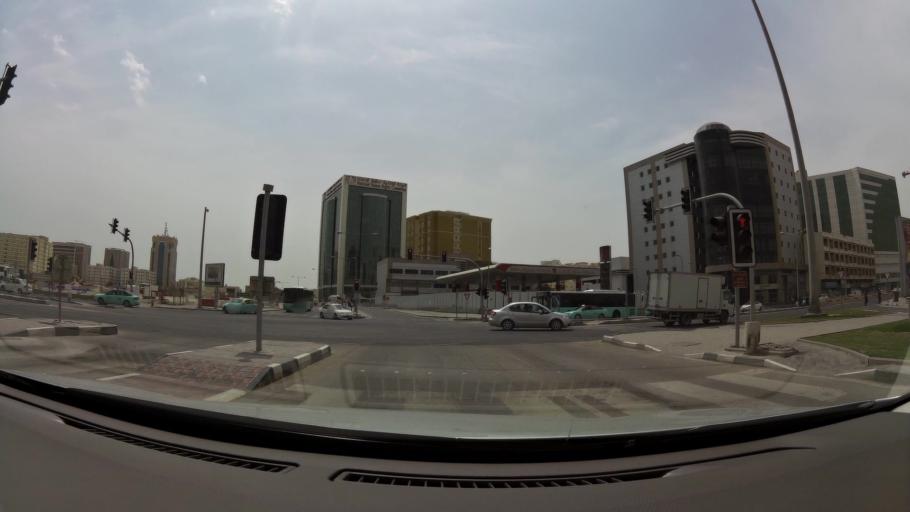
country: QA
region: Baladiyat ad Dawhah
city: Doha
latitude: 25.2799
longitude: 51.5285
